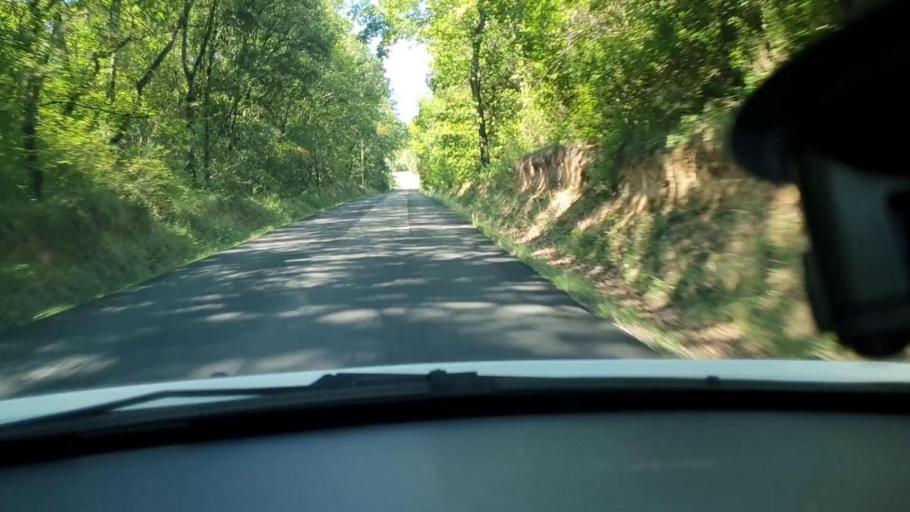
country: FR
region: Languedoc-Roussillon
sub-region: Departement du Gard
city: Goudargues
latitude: 44.1757
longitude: 4.5012
